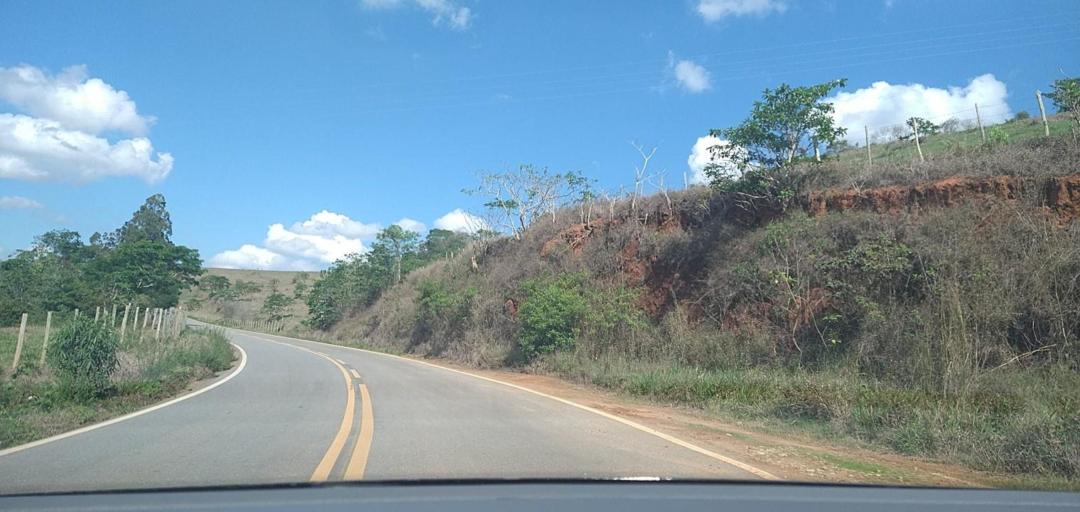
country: BR
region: Minas Gerais
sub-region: Alvinopolis
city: Alvinopolis
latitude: -20.0171
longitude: -43.0929
